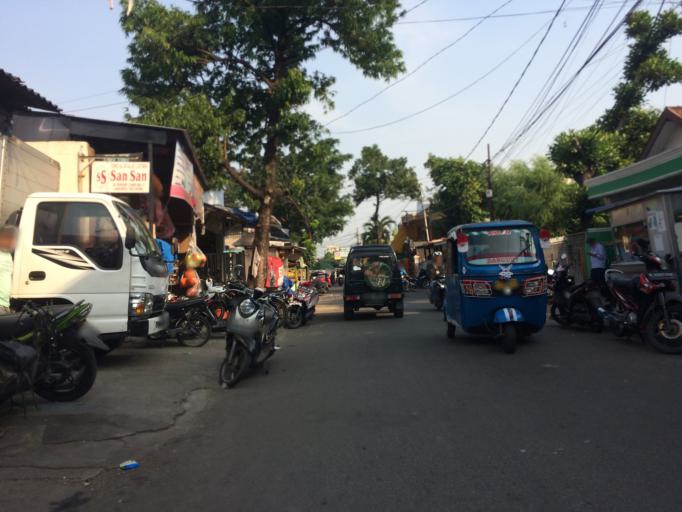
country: ID
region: Jakarta Raya
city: Jakarta
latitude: -6.2093
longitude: 106.8417
